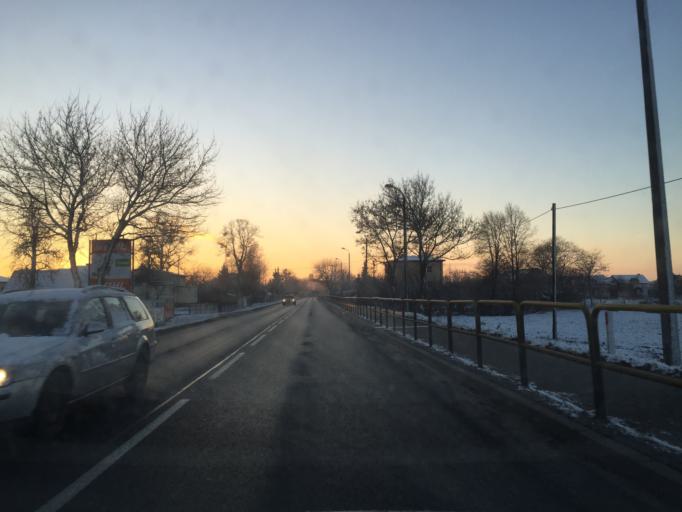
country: PL
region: Kujawsko-Pomorskie
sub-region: Powiat torunski
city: Lubicz Dolny
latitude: 53.0609
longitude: 18.7269
